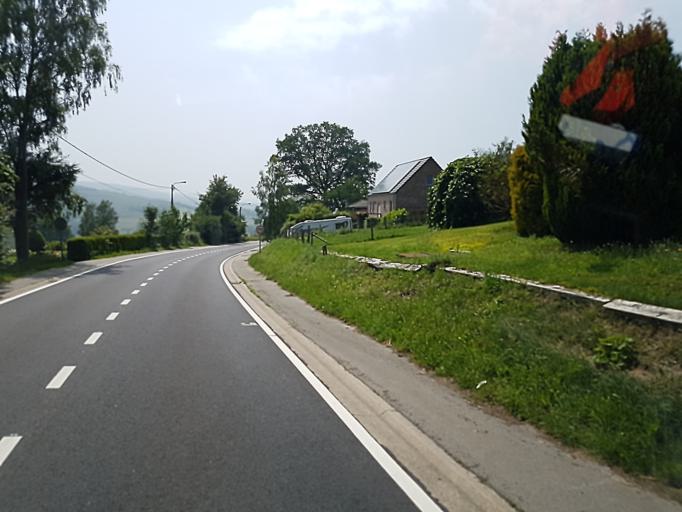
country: BE
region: Wallonia
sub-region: Province de Liege
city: Lierneux
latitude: 50.3307
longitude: 5.7714
